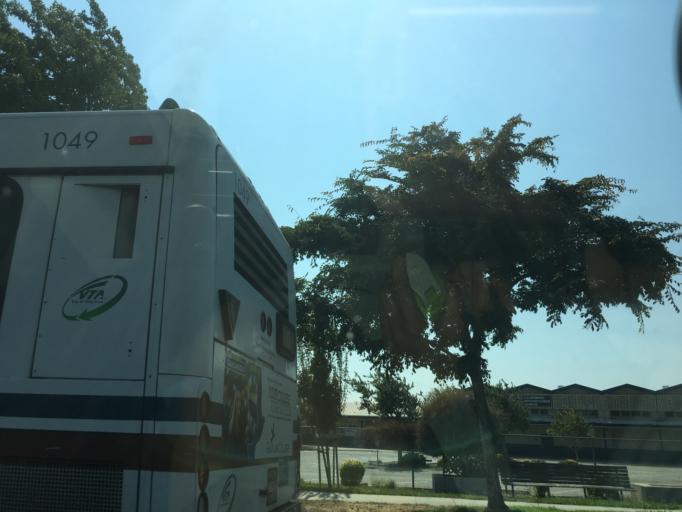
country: US
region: California
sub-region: Santa Clara County
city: East Foothills
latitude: 37.3934
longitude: -121.8439
